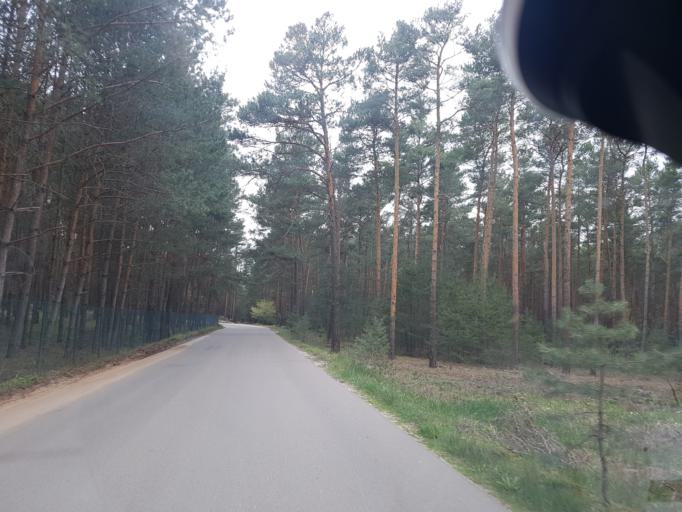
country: DE
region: Brandenburg
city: Linthe
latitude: 52.1628
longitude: 12.7724
